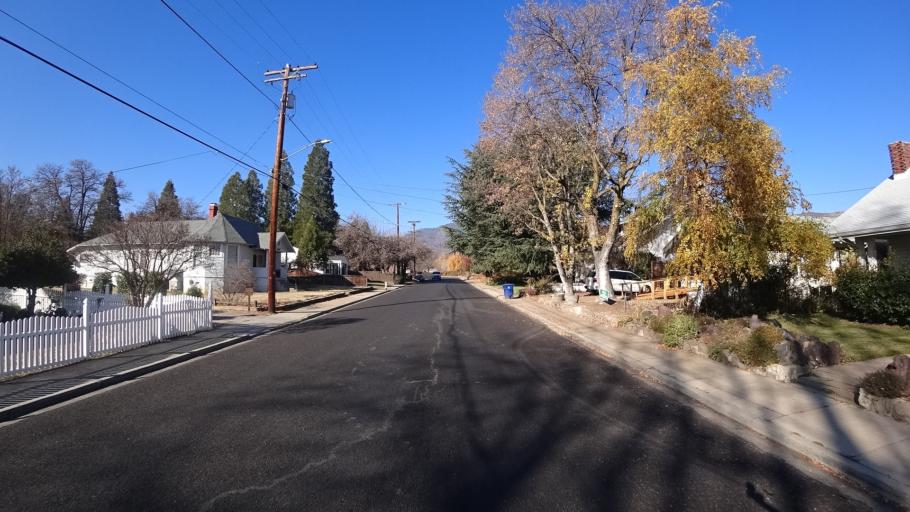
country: US
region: California
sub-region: Siskiyou County
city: Yreka
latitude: 41.7316
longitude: -122.6430
